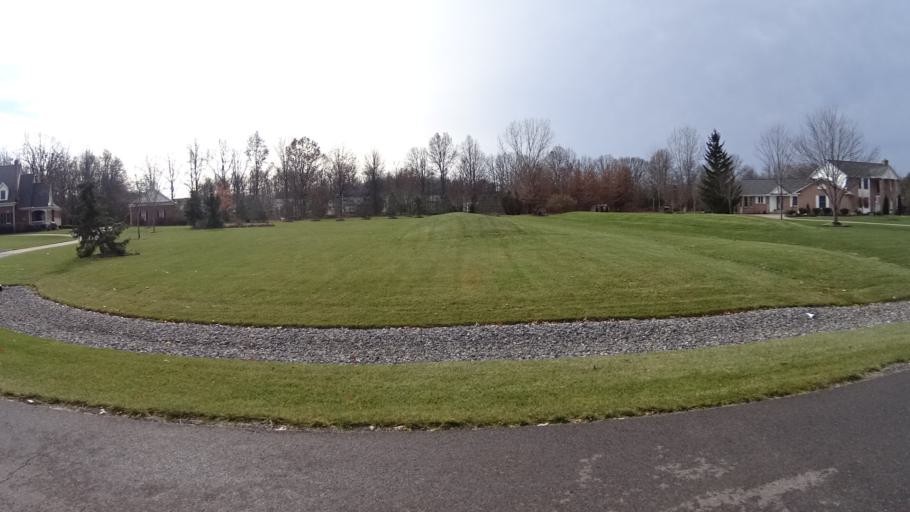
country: US
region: Ohio
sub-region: Lorain County
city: North Ridgeville
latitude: 41.3669
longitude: -82.0413
